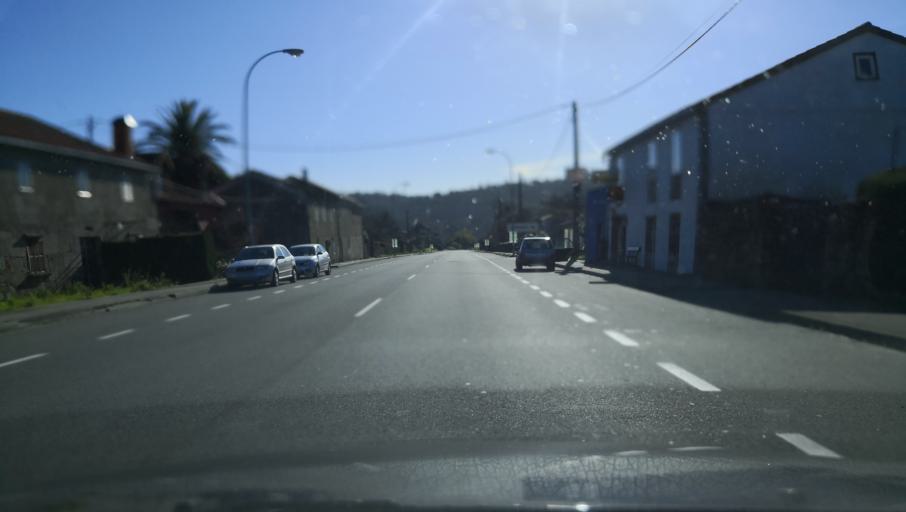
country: ES
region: Galicia
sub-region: Provincia de Pontevedra
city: Silleda
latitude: 42.7364
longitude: -8.3236
